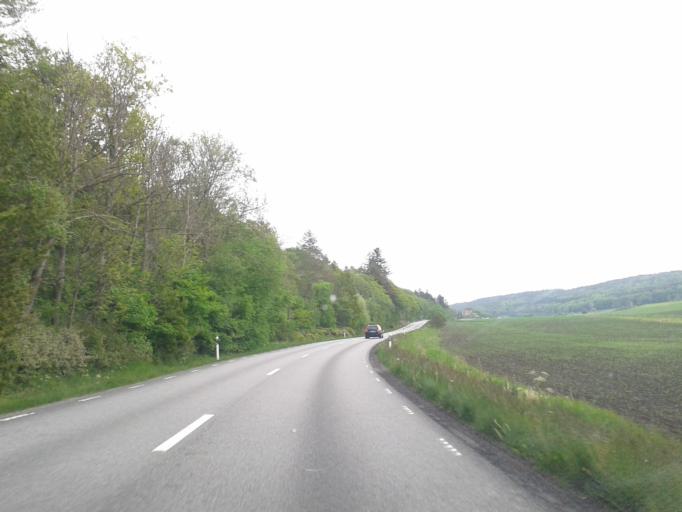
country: SE
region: Vaestra Goetaland
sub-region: Kungalvs Kommun
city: Kode
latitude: 57.8917
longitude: 11.7563
